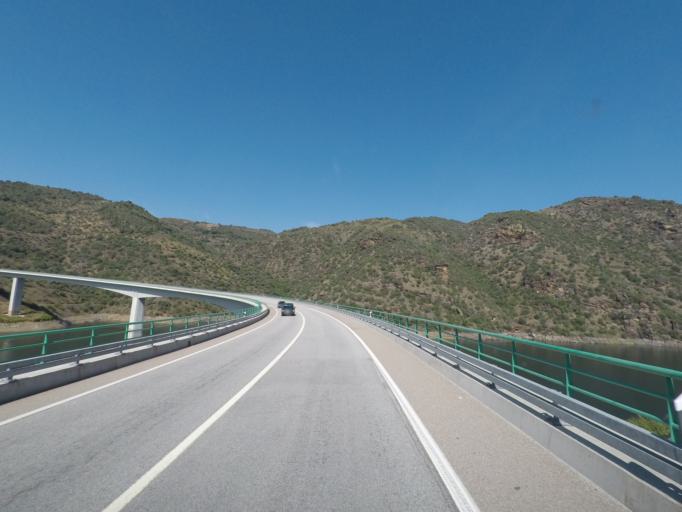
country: PT
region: Braganca
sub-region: Alfandega da Fe
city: Alfandega da Fe
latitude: 41.2865
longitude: -6.8720
